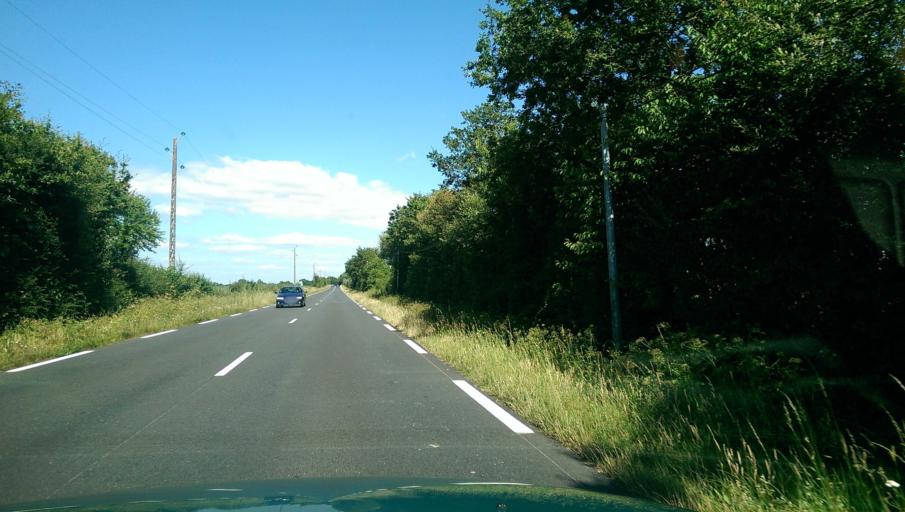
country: FR
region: Pays de la Loire
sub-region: Departement de la Vendee
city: Falleron
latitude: 46.8824
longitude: -1.6923
